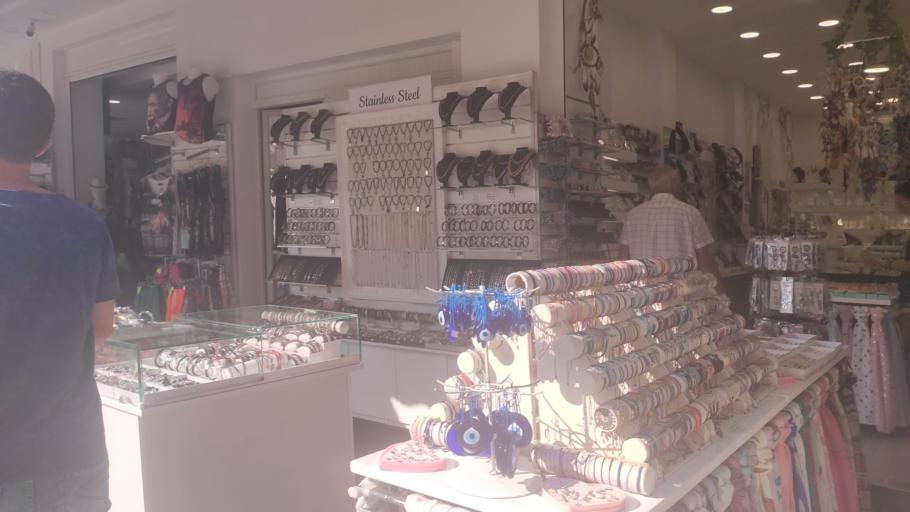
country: GR
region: South Aegean
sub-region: Nomos Dodekanisou
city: Kos
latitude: 36.8965
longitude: 27.2855
